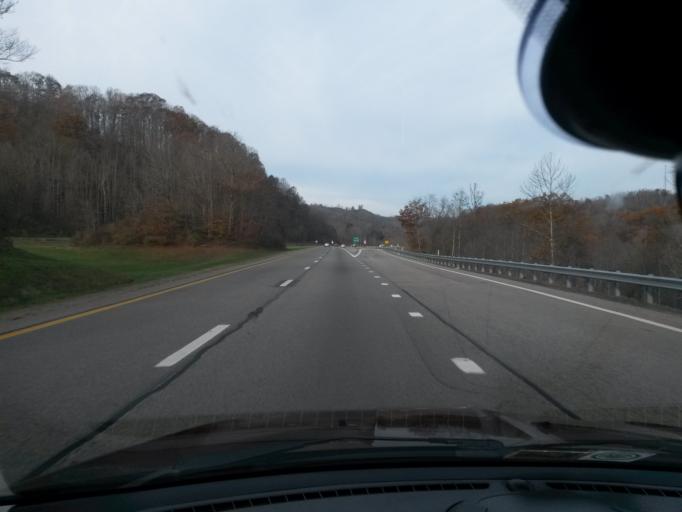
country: US
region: West Virginia
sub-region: Fayette County
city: Oak Hill
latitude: 37.9704
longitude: -81.2778
